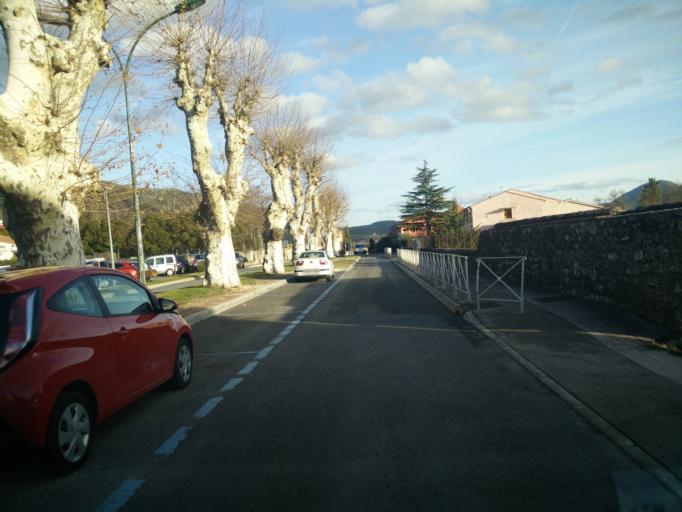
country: FR
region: Provence-Alpes-Cote d'Azur
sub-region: Departement du Var
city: Signes
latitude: 43.2906
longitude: 5.8658
